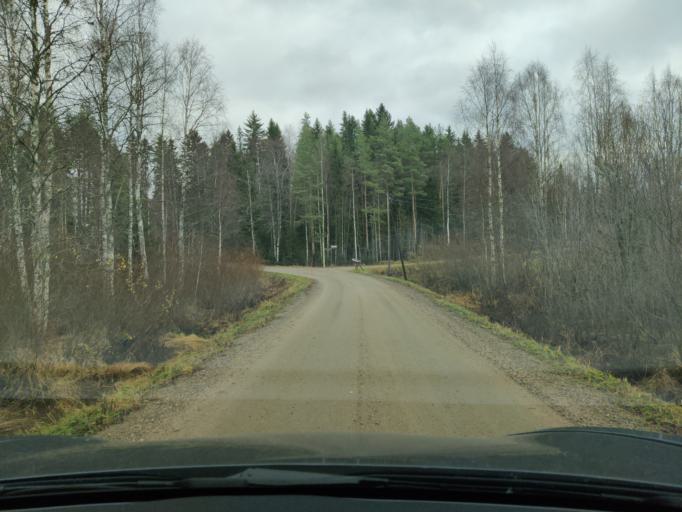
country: FI
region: Northern Savo
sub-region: Ylae-Savo
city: Kiuruvesi
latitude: 63.6383
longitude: 26.6531
